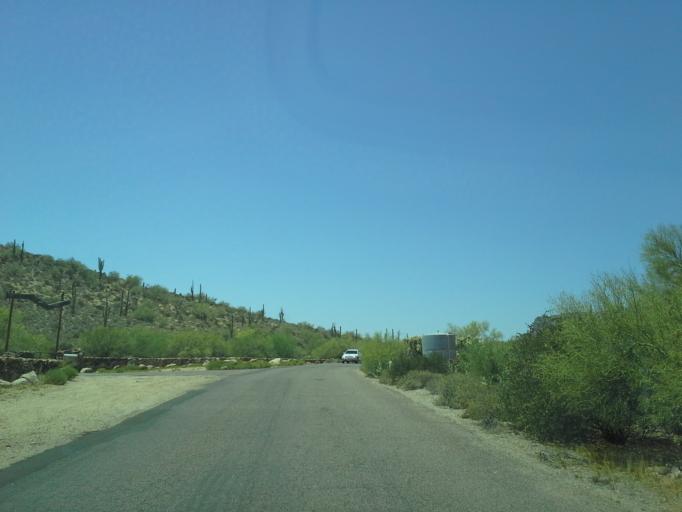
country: US
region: Arizona
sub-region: Pinal County
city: Apache Junction
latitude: 33.3849
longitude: -111.4321
